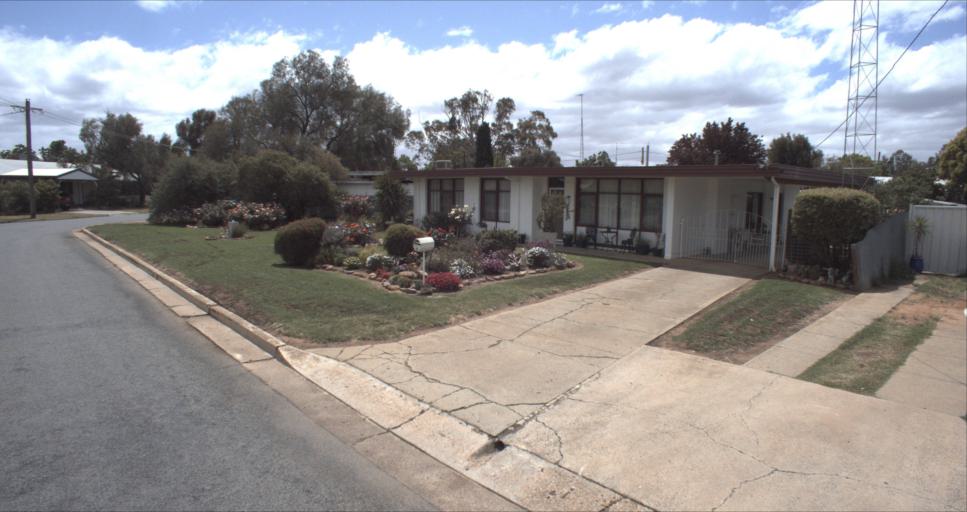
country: AU
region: New South Wales
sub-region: Leeton
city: Leeton
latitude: -34.5552
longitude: 146.3897
